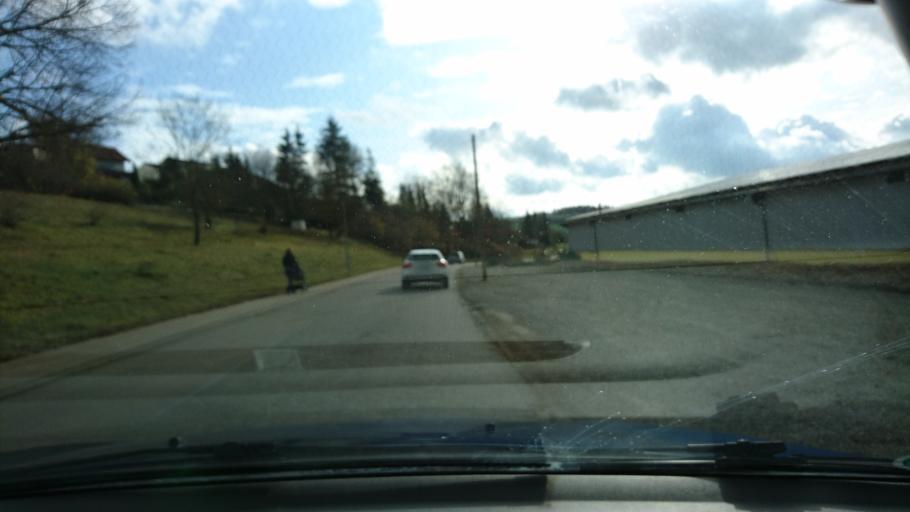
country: DE
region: Baden-Wuerttemberg
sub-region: Regierungsbezirk Stuttgart
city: Neresheim
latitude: 48.7582
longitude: 10.3177
